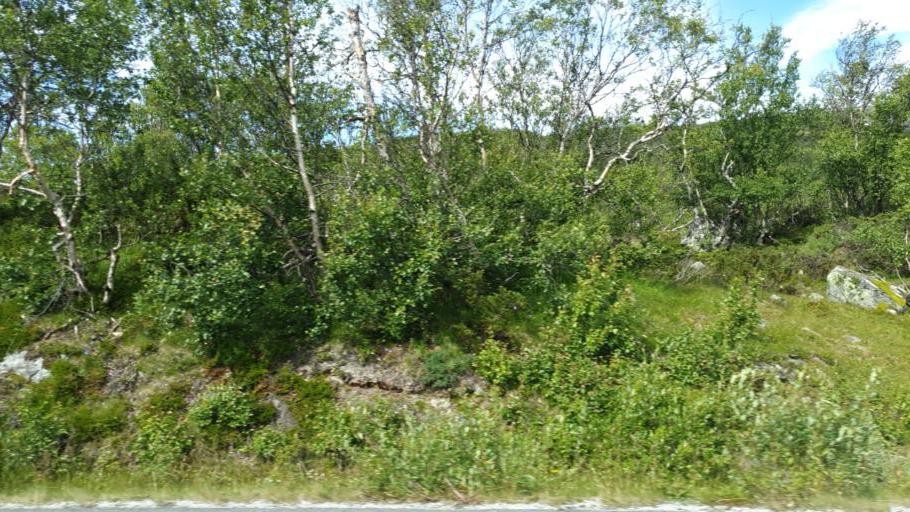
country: NO
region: Oppland
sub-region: Oystre Slidre
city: Heggenes
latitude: 61.4921
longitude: 8.8421
